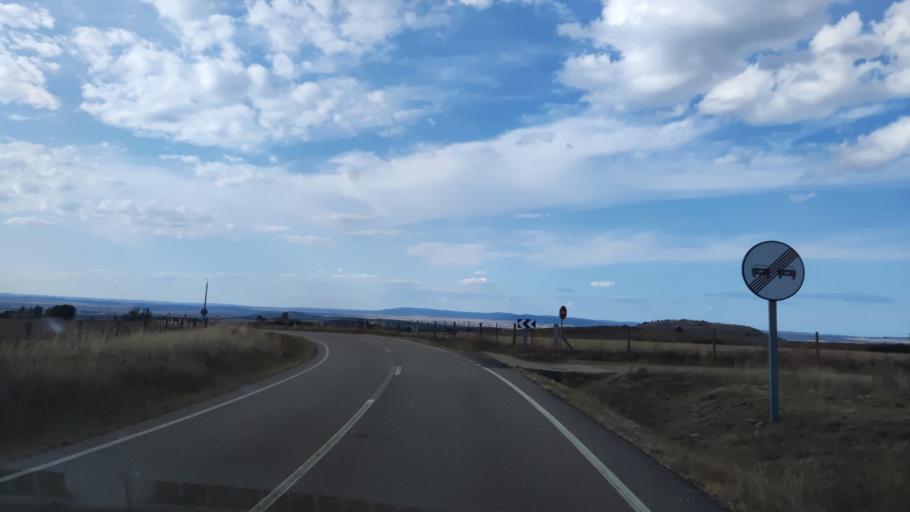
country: ES
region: Castille and Leon
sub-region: Provincia de Salamanca
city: Pastores
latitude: 40.5124
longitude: -6.5055
